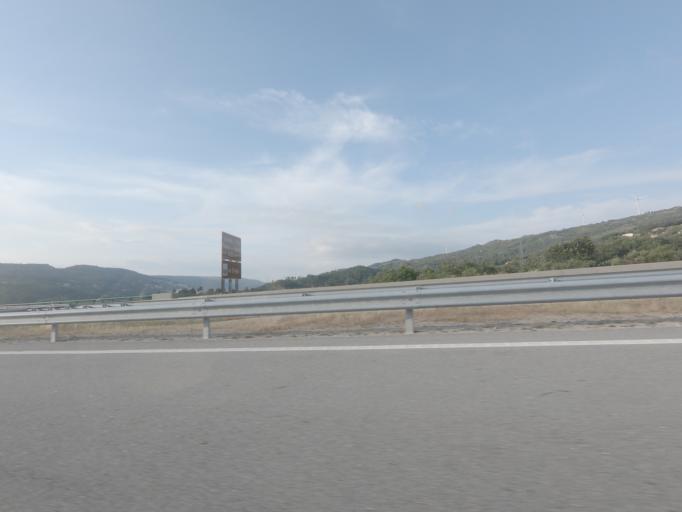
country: PT
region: Vila Real
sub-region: Vila Pouca de Aguiar
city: Vila Pouca de Aguiar
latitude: 41.4784
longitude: -7.6479
